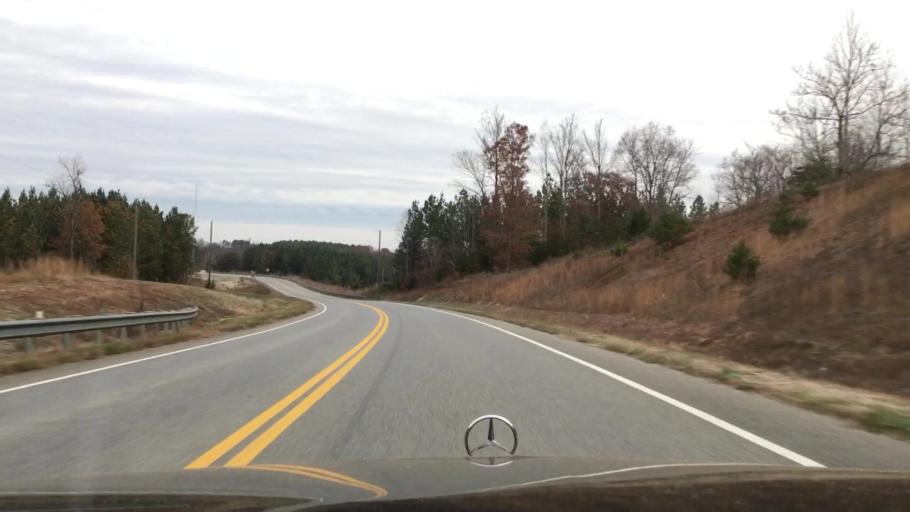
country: US
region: Virginia
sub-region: Campbell County
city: Altavista
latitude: 37.1900
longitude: -79.2936
